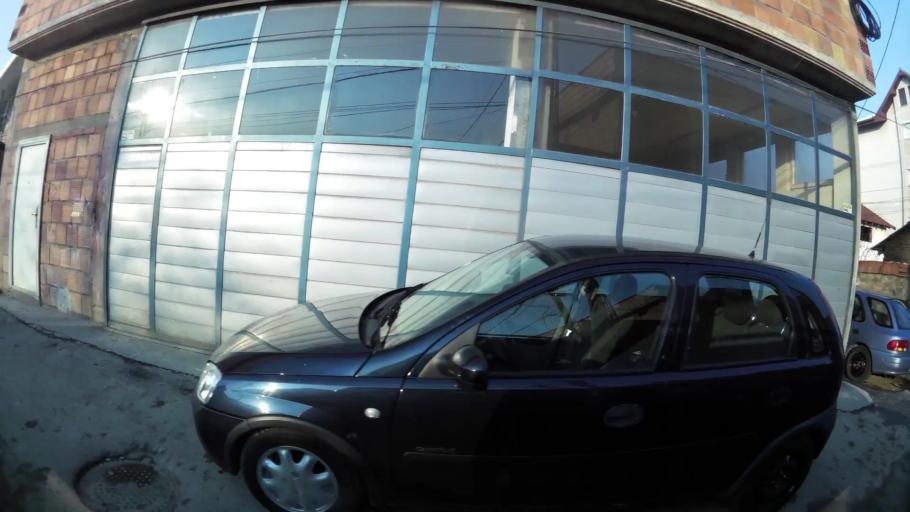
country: MK
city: Creshevo
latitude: 42.0192
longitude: 21.5152
